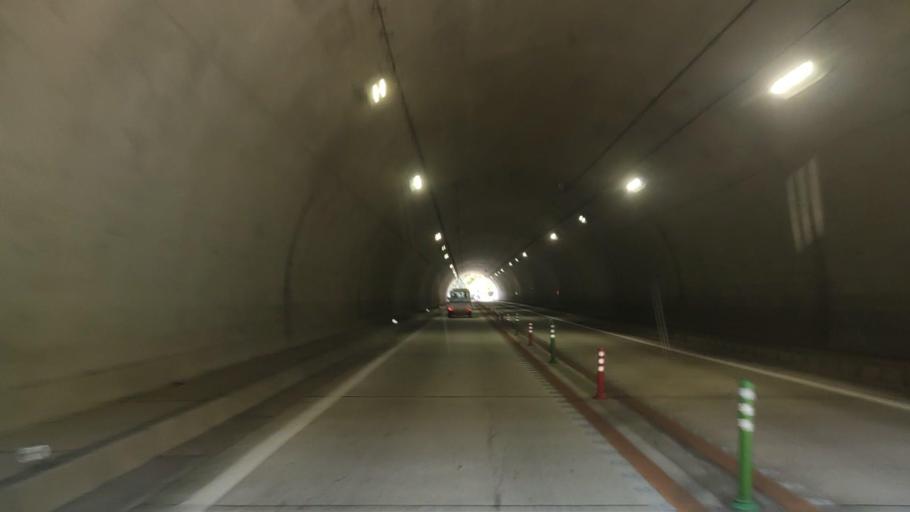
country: JP
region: Wakayama
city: Tanabe
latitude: 33.6422
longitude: 135.4096
